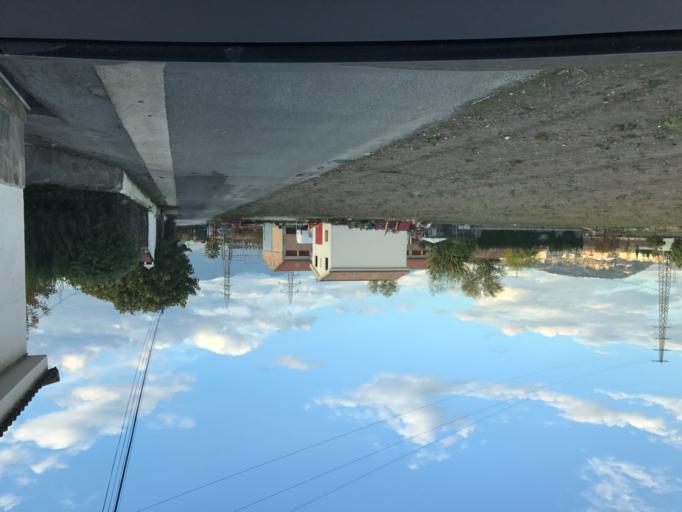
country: ES
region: Andalusia
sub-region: Provincia de Granada
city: Granada
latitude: 37.1773
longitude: -3.6231
